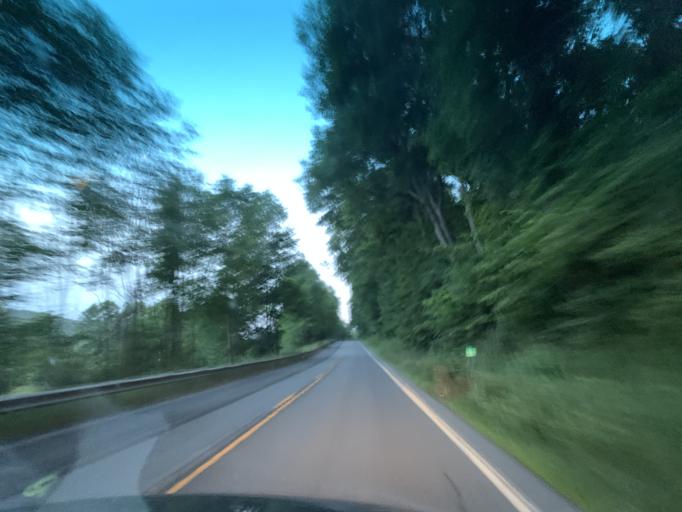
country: US
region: New York
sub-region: Chenango County
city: New Berlin
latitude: 42.6636
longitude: -75.3322
